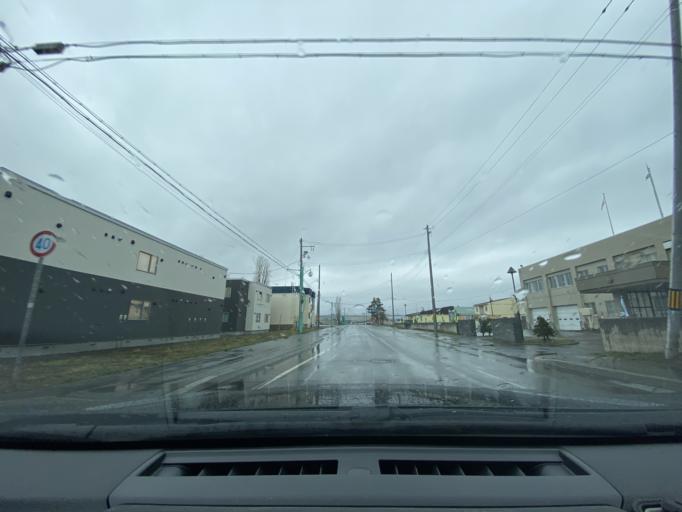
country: JP
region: Hokkaido
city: Fukagawa
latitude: 43.8093
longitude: 141.9291
